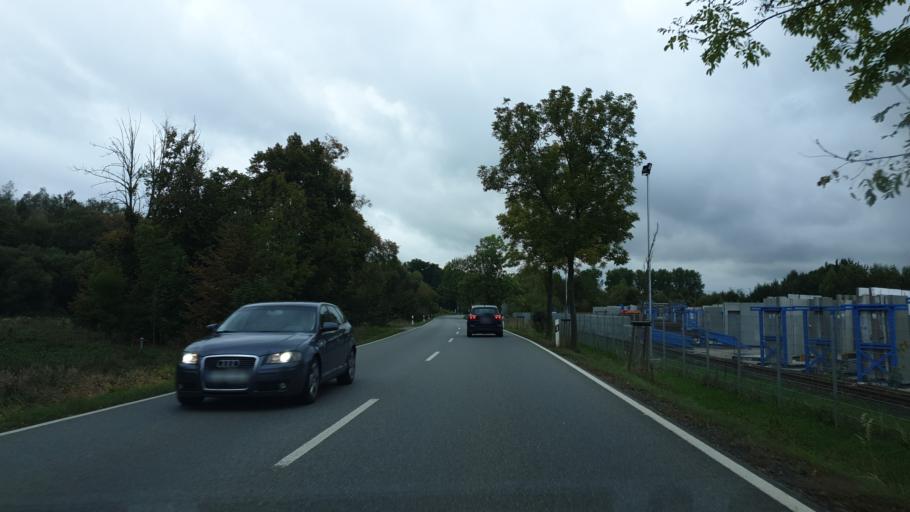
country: DE
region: Saxony
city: Glauchau
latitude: 50.8269
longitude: 12.5592
